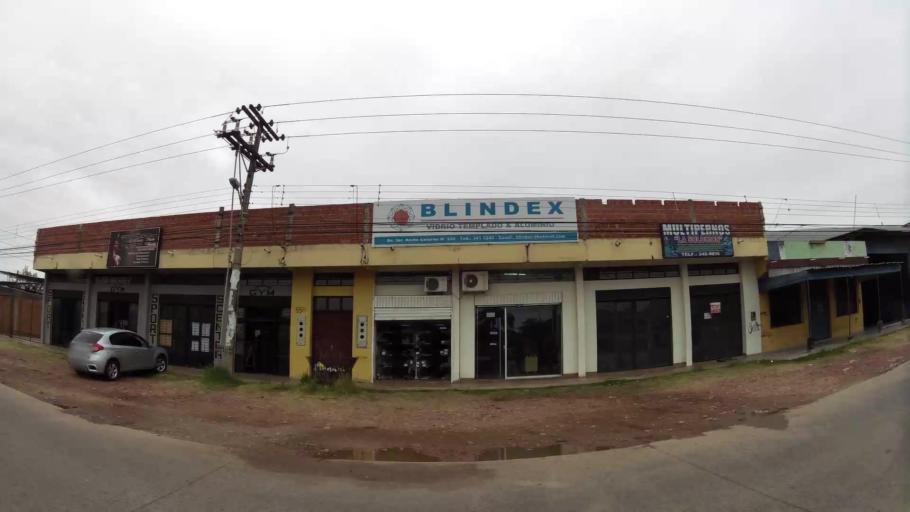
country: BO
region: Santa Cruz
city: Santa Cruz de la Sierra
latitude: -17.7579
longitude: -63.1805
